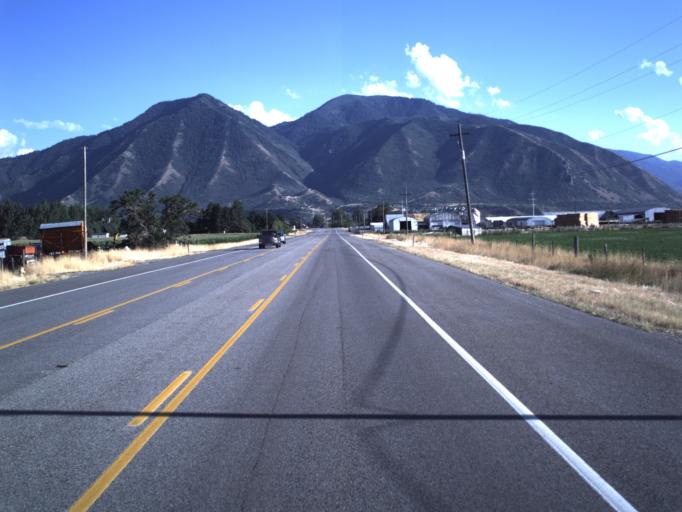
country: US
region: Utah
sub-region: Utah County
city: Mapleton
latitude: 40.1113
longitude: -111.5978
